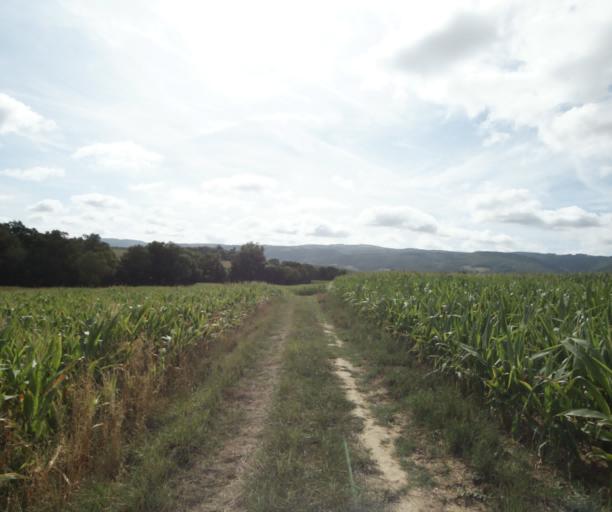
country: FR
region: Midi-Pyrenees
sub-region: Departement du Tarn
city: Soreze
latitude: 43.4870
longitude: 2.0908
